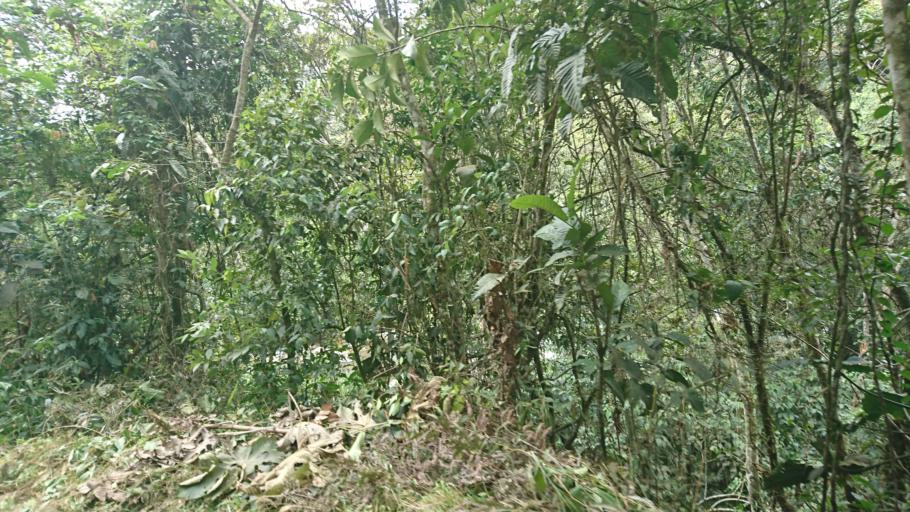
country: BO
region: La Paz
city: Coroico
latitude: -16.1132
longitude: -67.7888
